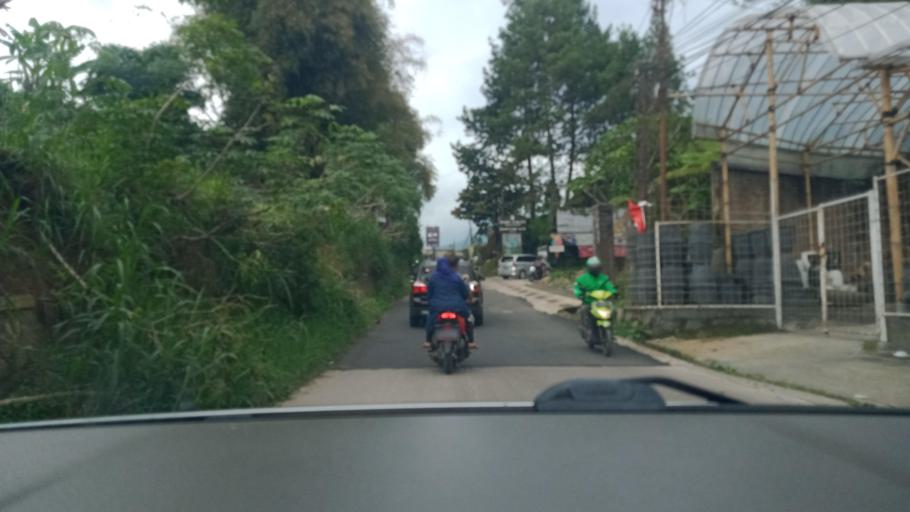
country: ID
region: West Java
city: Lembang
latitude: -6.8230
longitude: 107.5972
